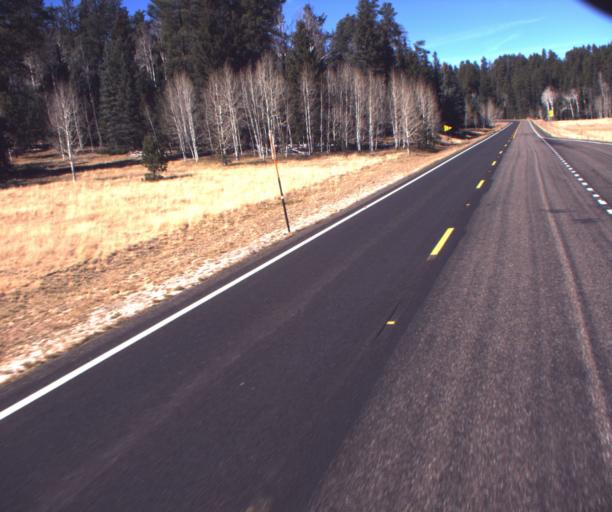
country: US
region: Arizona
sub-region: Coconino County
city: Grand Canyon
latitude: 36.5310
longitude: -112.1510
